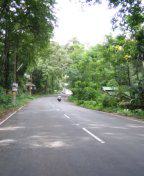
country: IN
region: Kerala
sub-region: Thrissur District
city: Trichur
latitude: 10.5269
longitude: 76.3503
